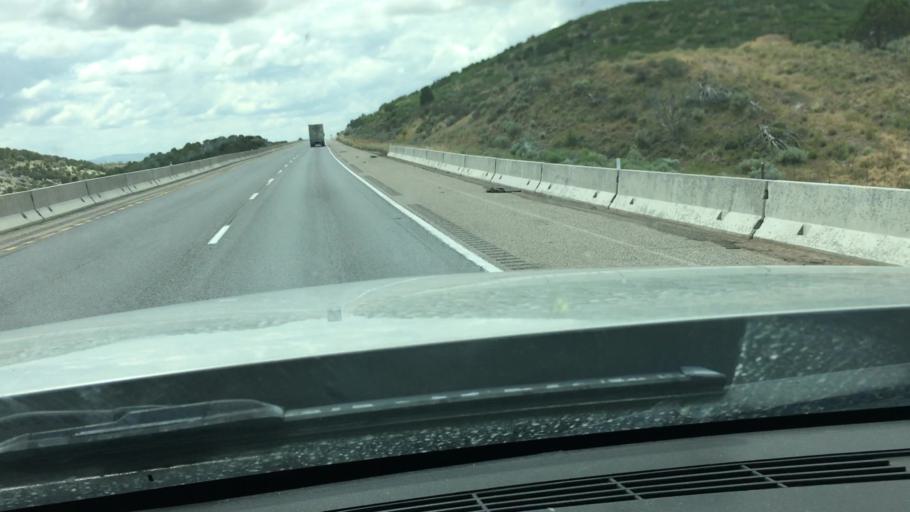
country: US
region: Utah
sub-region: Beaver County
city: Beaver
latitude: 38.4569
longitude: -112.6230
